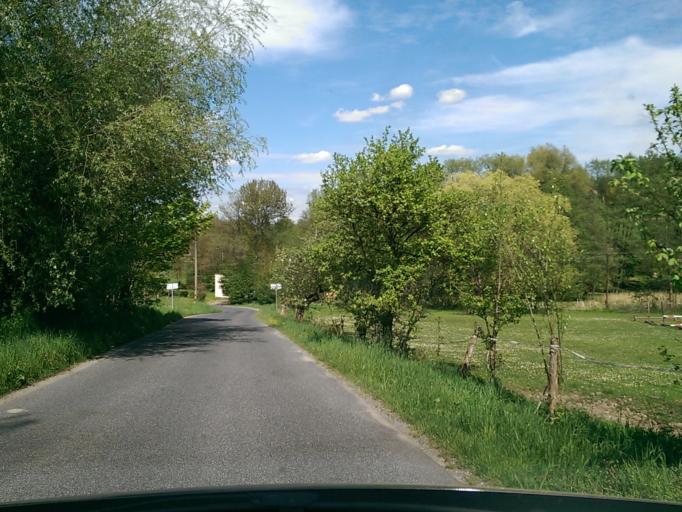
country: CZ
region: Liberecky
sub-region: Okres Semily
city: Turnov
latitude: 50.5664
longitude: 15.1409
